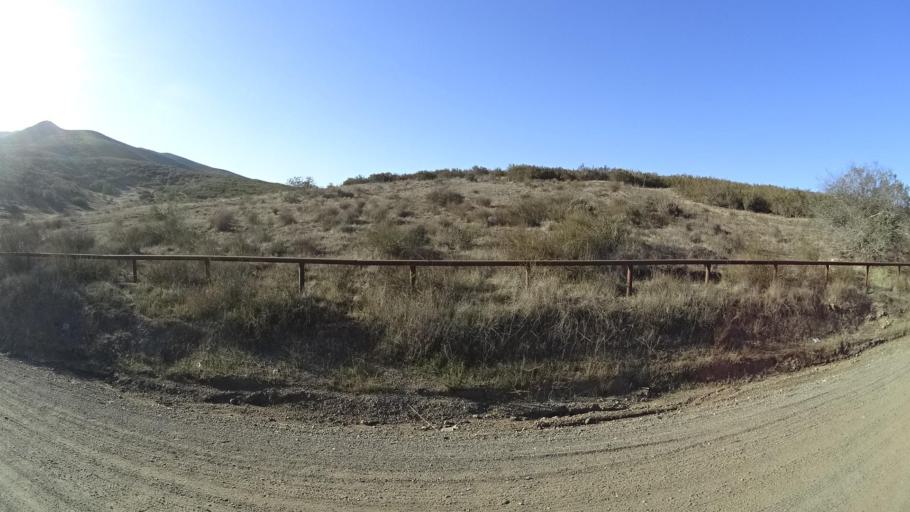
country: US
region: California
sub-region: San Diego County
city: Jamul
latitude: 32.6925
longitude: -116.9035
